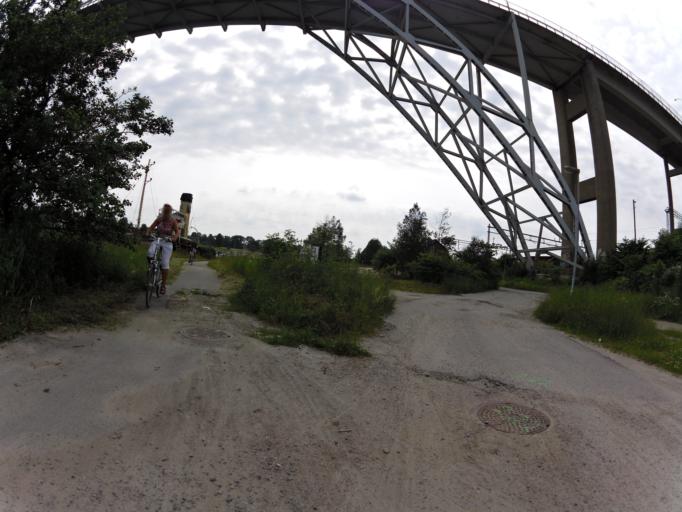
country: NO
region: Ostfold
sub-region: Fredrikstad
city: Fredrikstad
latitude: 59.2111
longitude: 10.9594
